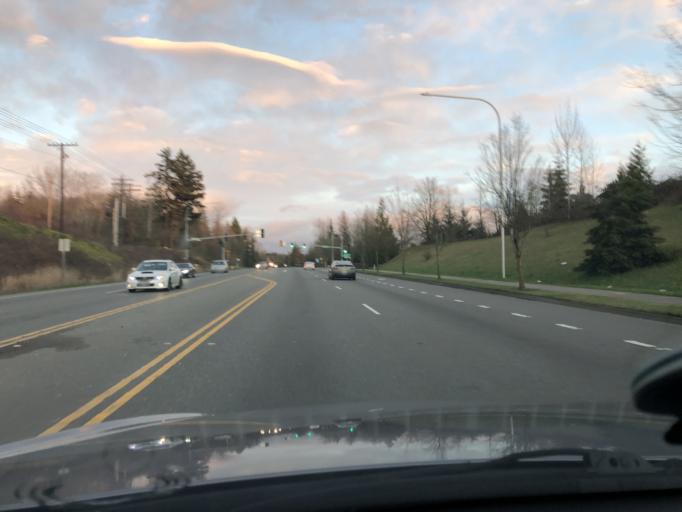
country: US
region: Washington
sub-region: King County
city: Federal Way
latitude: 47.3151
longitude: -122.2941
